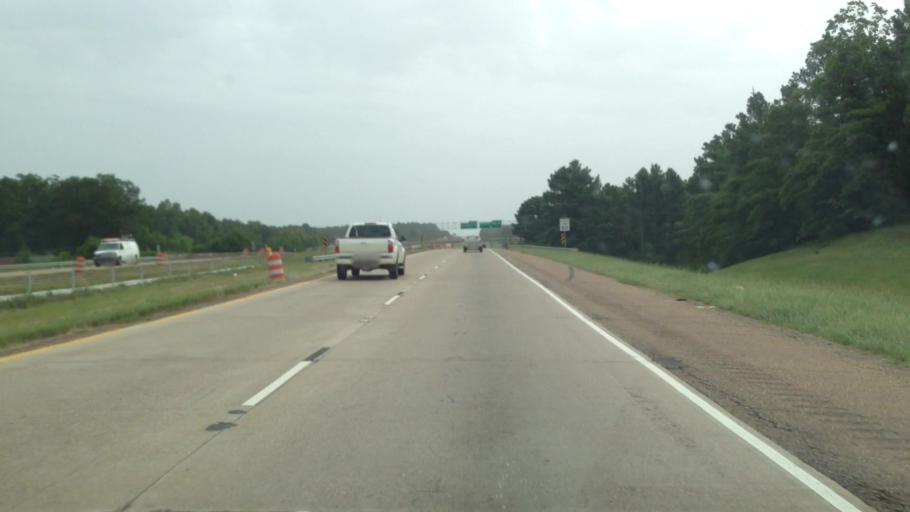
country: US
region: Louisiana
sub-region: Caddo Parish
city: Shreveport
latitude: 32.4679
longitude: -93.8410
